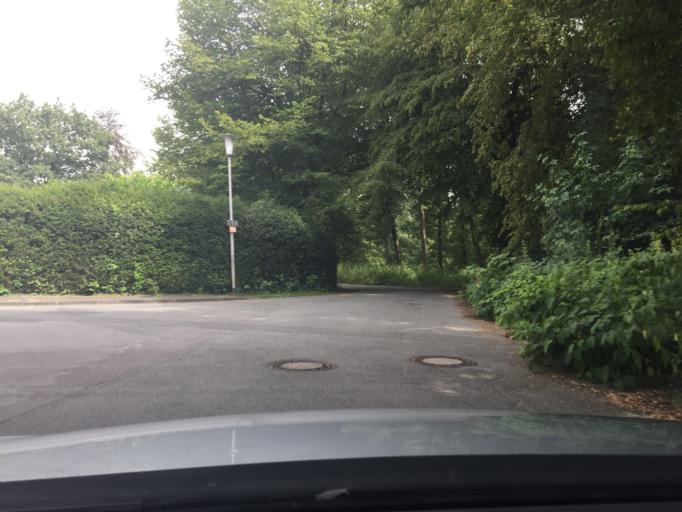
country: DE
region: North Rhine-Westphalia
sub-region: Regierungsbezirk Dusseldorf
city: Ratingen
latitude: 51.3366
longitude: 6.8891
